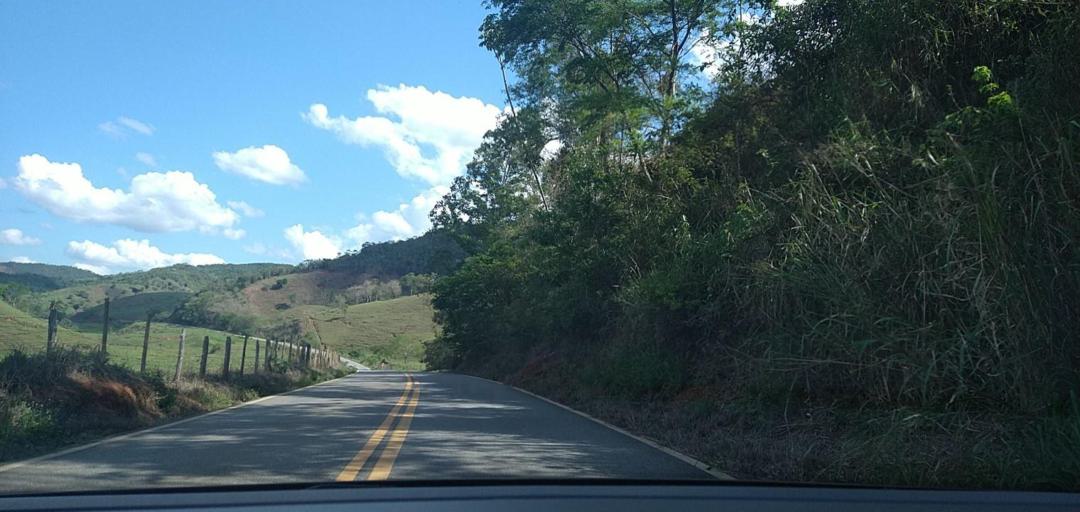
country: BR
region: Minas Gerais
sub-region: Rio Piracicaba
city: Rio Piracicaba
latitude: -19.9839
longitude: -43.1228
